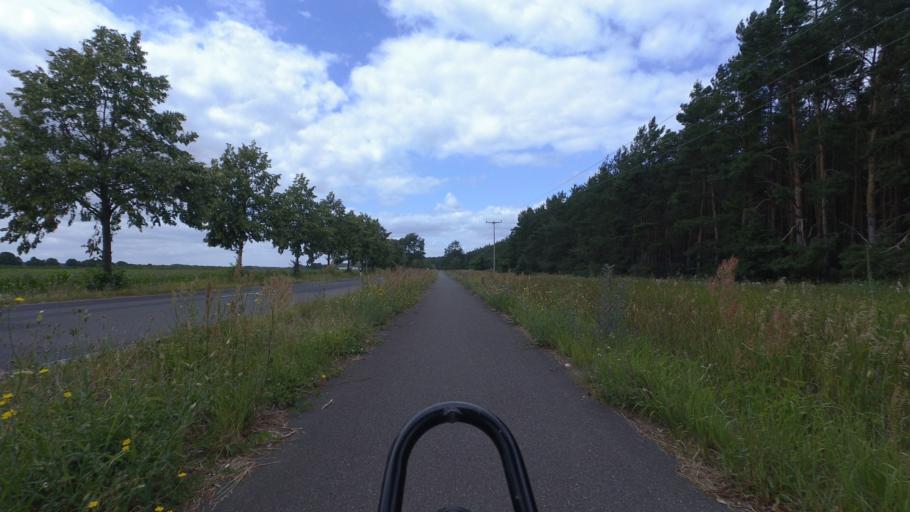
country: DE
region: Brandenburg
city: Trebbin
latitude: 52.2336
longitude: 13.1933
